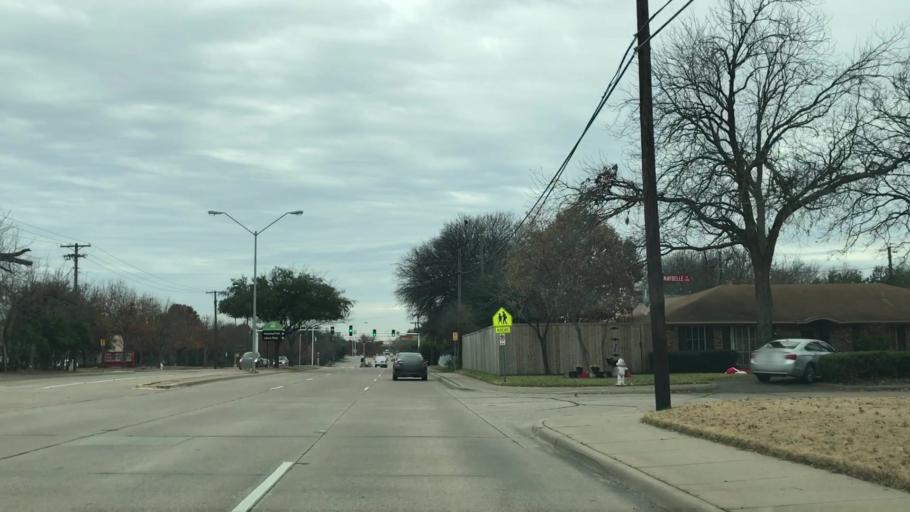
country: US
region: Texas
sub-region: Dallas County
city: Farmers Branch
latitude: 32.9187
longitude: -96.8818
